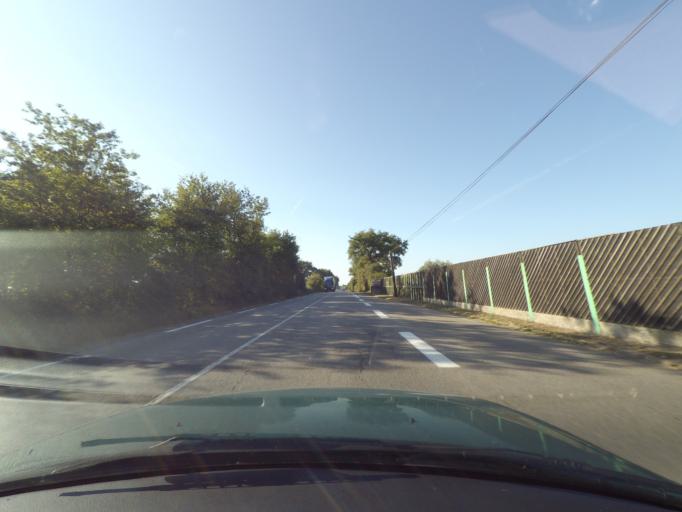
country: FR
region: Poitou-Charentes
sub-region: Departement des Deux-Sevres
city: Chiche
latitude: 46.7532
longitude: -0.3084
